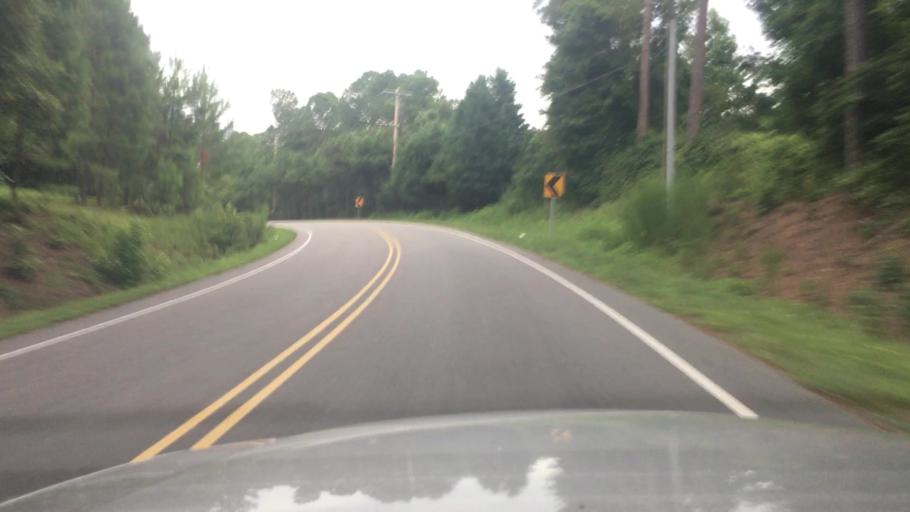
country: US
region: North Carolina
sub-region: Hoke County
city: Rockfish
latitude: 34.9911
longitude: -79.0243
